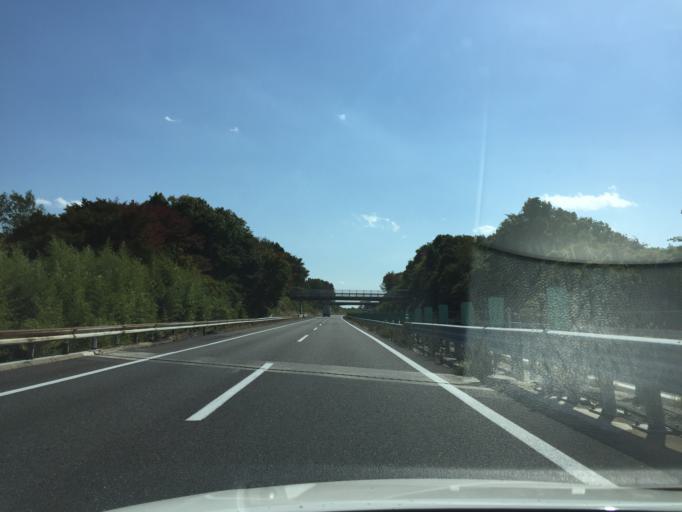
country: JP
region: Fukushima
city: Sukagawa
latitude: 37.3246
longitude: 140.3400
